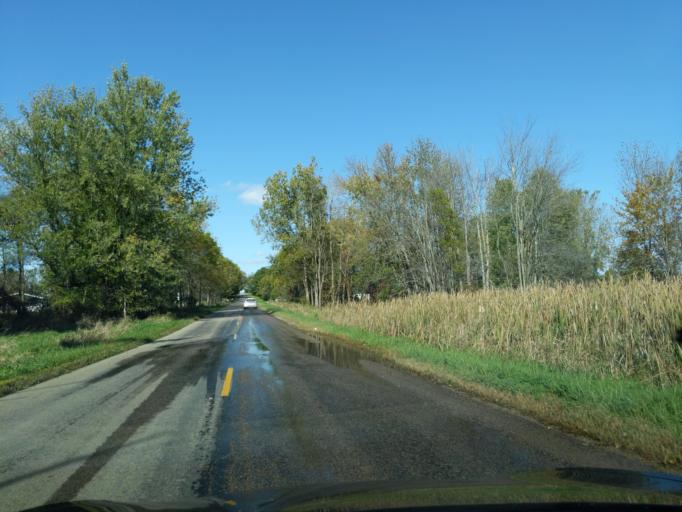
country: US
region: Michigan
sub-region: Eaton County
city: Charlotte
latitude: 42.6035
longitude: -84.7979
